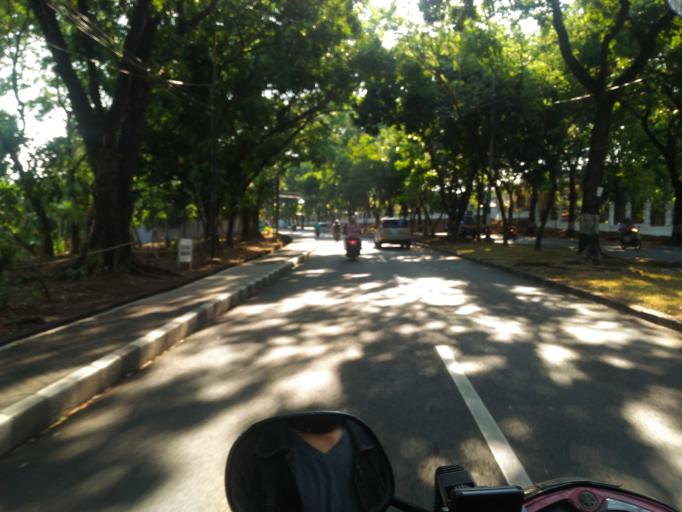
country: ID
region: West Java
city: Depok
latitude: -6.3183
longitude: 106.8533
